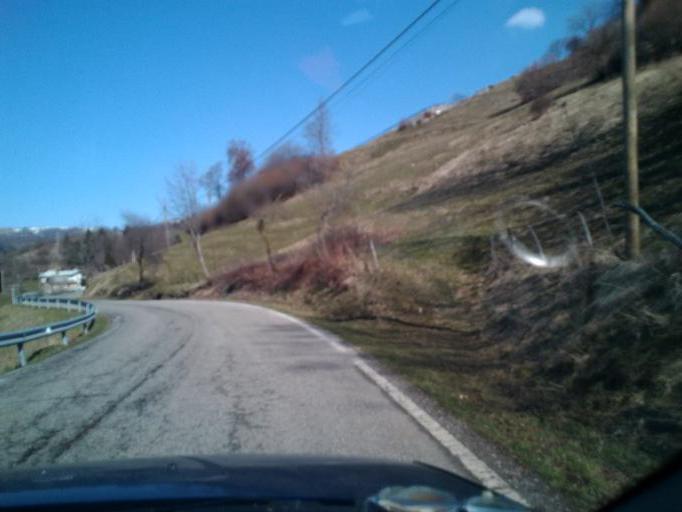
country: IT
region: Veneto
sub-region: Provincia di Verona
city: Bosco Chiesanuova
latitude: 45.6424
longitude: 11.0263
